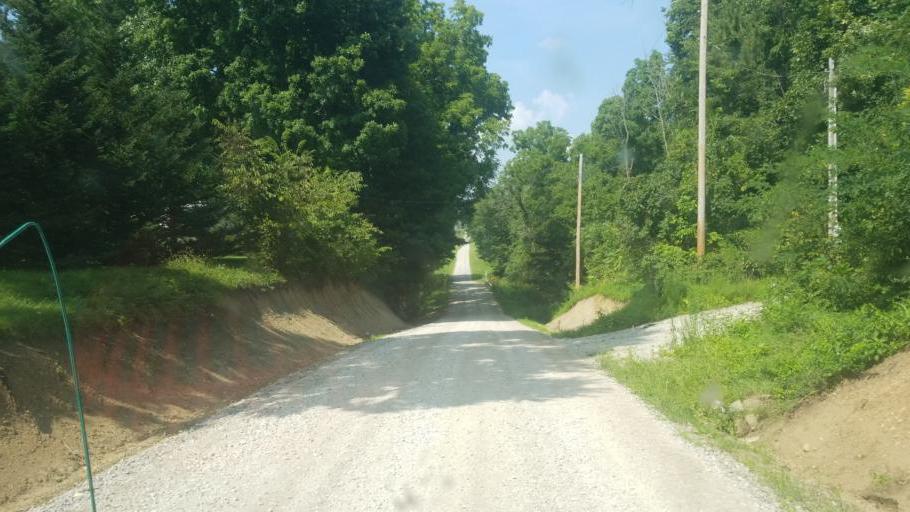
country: US
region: Ohio
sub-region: Huron County
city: New London
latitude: 41.0587
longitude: -82.4097
